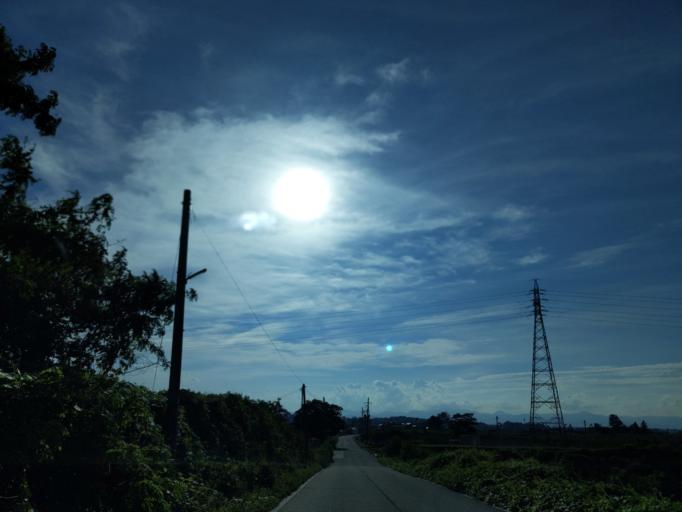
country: JP
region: Fukushima
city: Sukagawa
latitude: 37.2873
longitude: 140.4131
